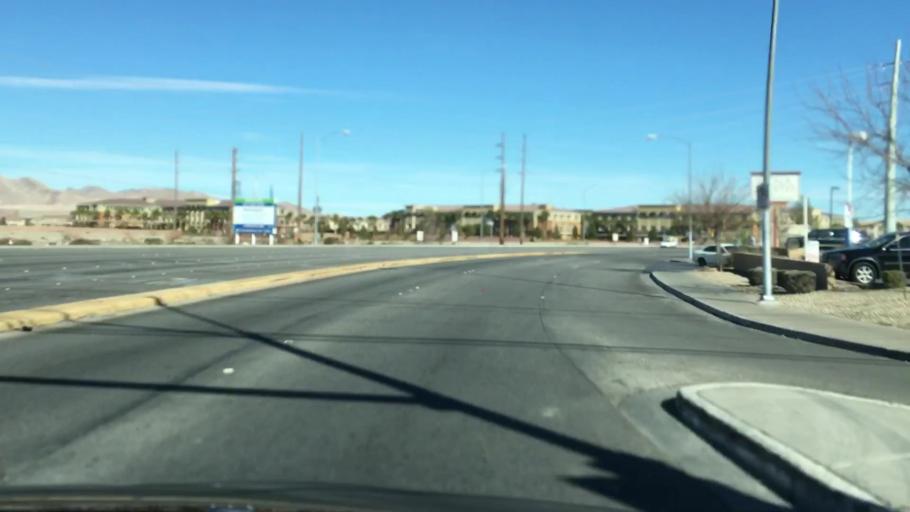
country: US
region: Nevada
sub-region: Clark County
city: Whitney
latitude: 36.0848
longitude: -115.0324
